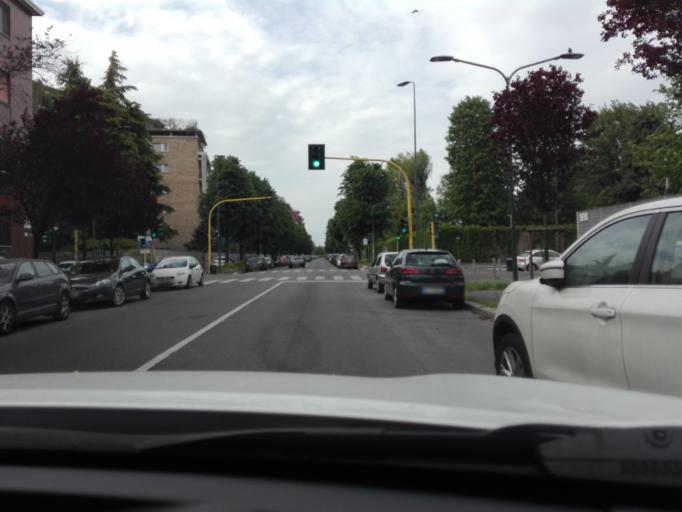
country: IT
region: Lombardy
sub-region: Citta metropolitana di Milano
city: Romano Banco
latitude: 45.4617
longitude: 9.1448
